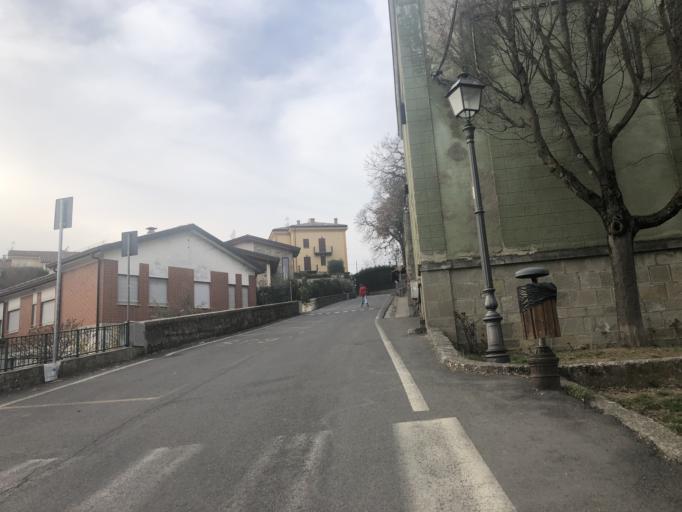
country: IT
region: Emilia-Romagna
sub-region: Provincia di Piacenza
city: Bobbio
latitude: 44.7672
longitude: 9.3830
